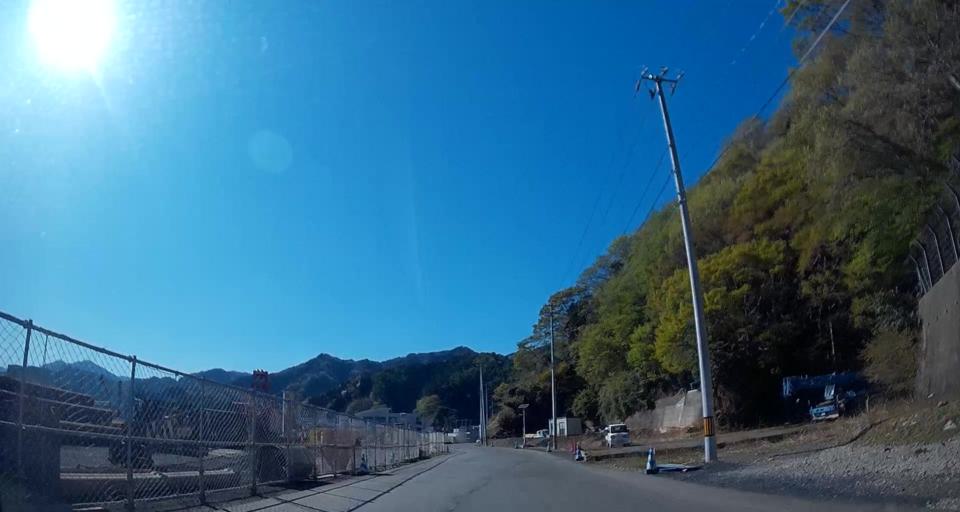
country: JP
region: Iwate
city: Kamaishi
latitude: 39.2722
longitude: 141.8949
